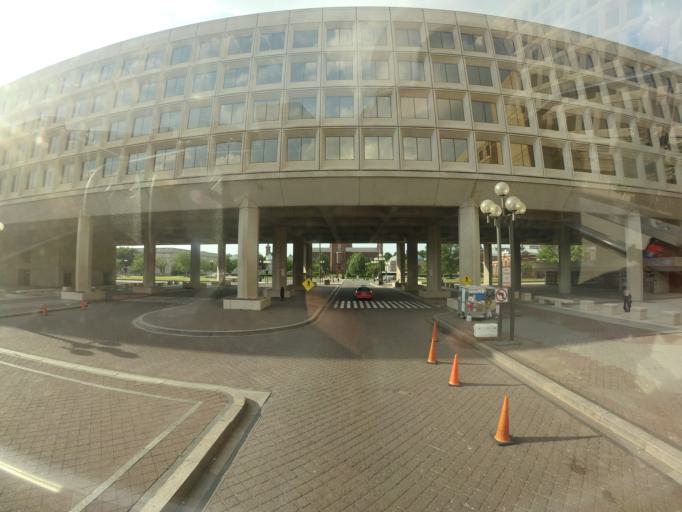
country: US
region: Washington, D.C.
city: Washington, D.C.
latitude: 38.8867
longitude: -77.0260
